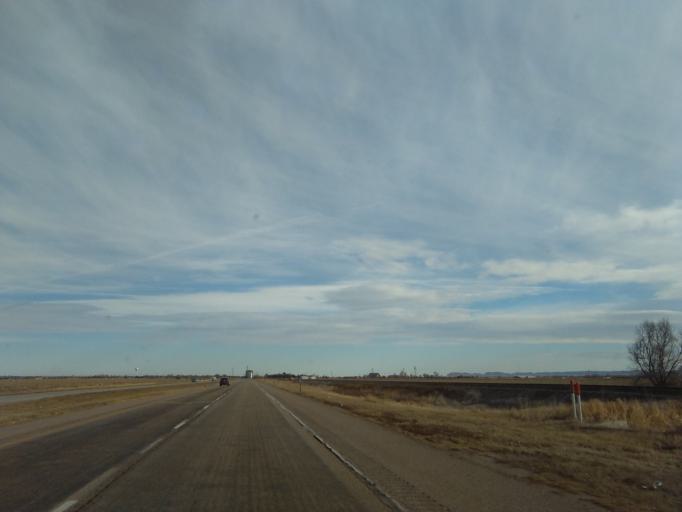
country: US
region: Nebraska
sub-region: Scotts Bluff County
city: Gering
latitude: 41.8190
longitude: -103.5387
